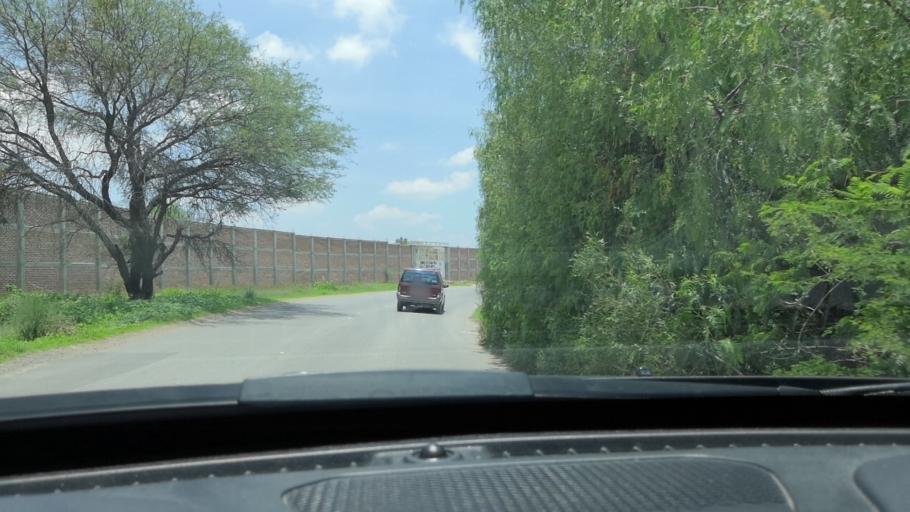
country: MX
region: Guanajuato
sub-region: Leon
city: Ladrilleras del Refugio
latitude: 21.0511
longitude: -101.5638
